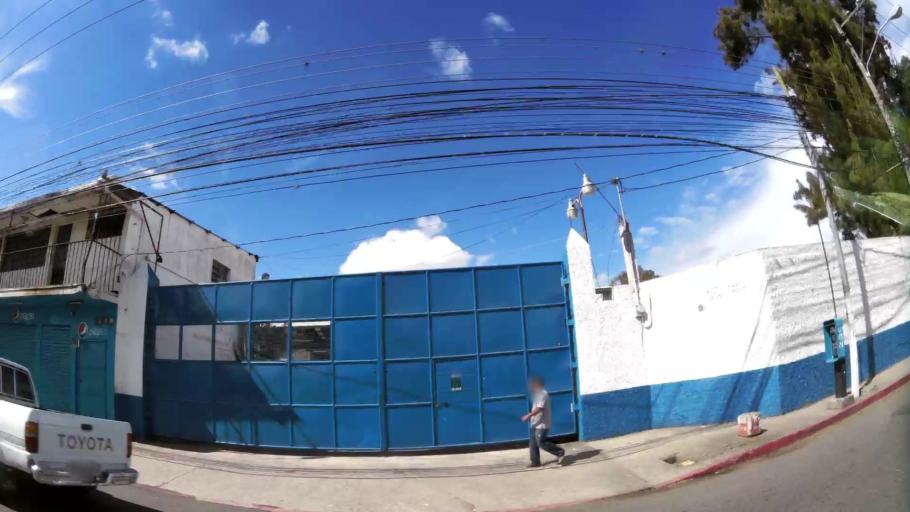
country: GT
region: Guatemala
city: Mixco
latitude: 14.6366
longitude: -90.5646
